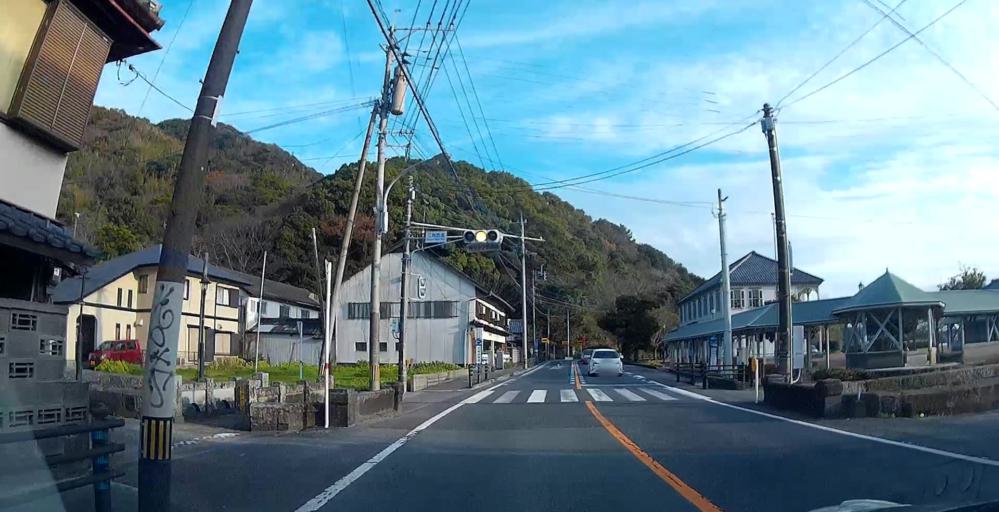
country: JP
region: Nagasaki
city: Shimabara
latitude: 32.6227
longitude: 130.4562
